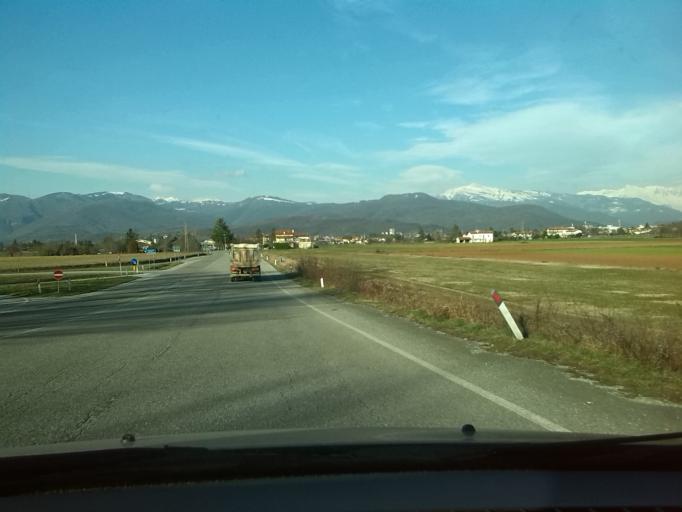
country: IT
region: Friuli Venezia Giulia
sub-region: Provincia di Udine
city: Cividale del Friuli
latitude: 46.0748
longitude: 13.4211
